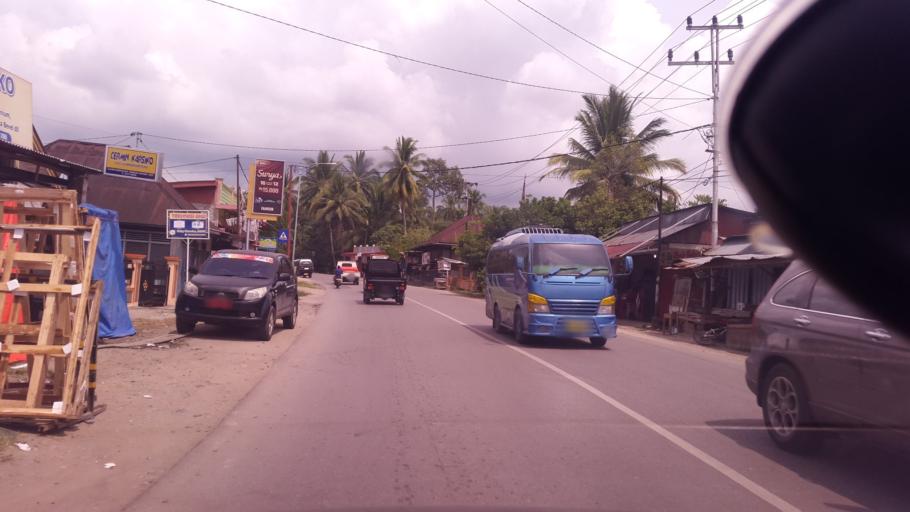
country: ID
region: West Sumatra
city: Solok
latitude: -0.8213
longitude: 100.6556
